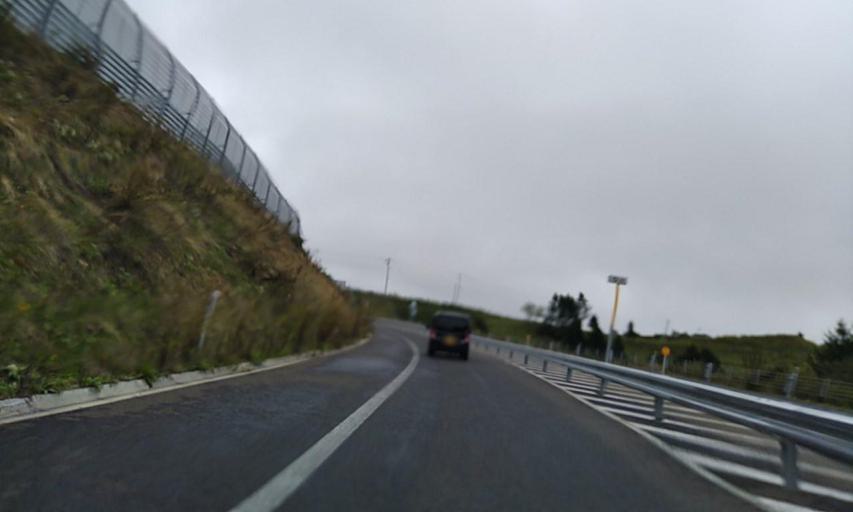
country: JP
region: Hokkaido
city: Nemuro
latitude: 43.2749
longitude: 145.5058
